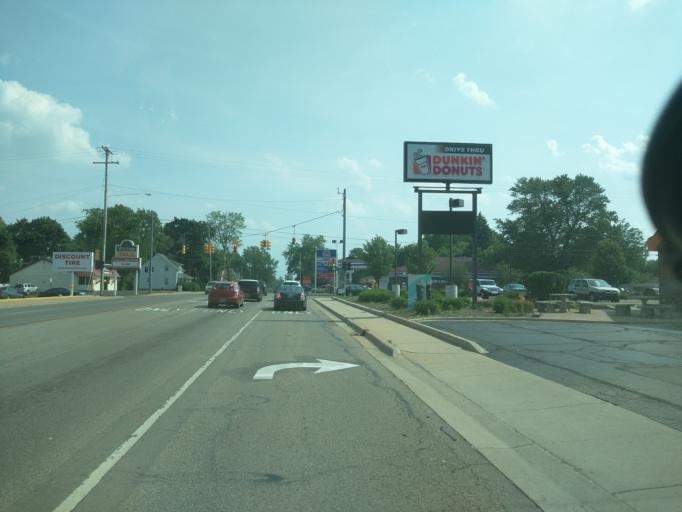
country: US
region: Michigan
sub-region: Jackson County
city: Jackson
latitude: 42.2595
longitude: -84.4235
